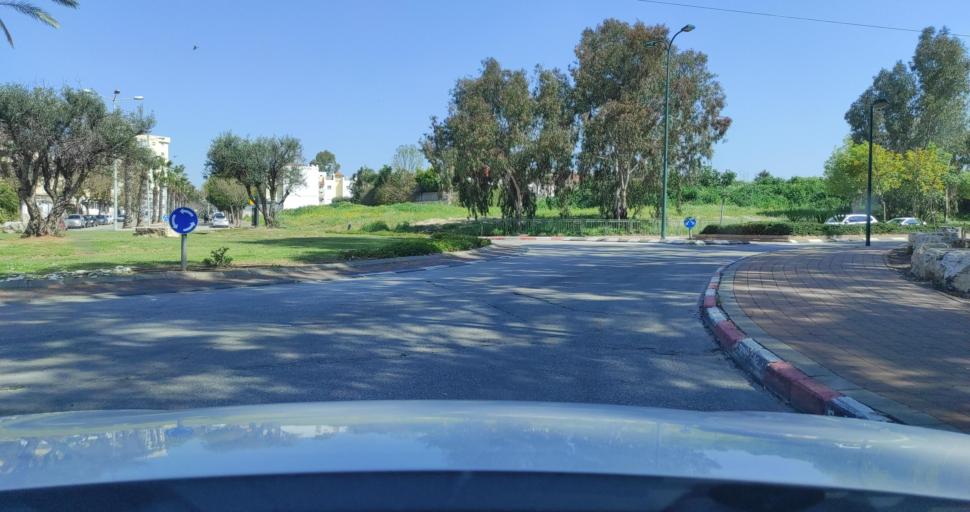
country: IL
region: Central District
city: Nordiyya
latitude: 32.3068
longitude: 34.8805
